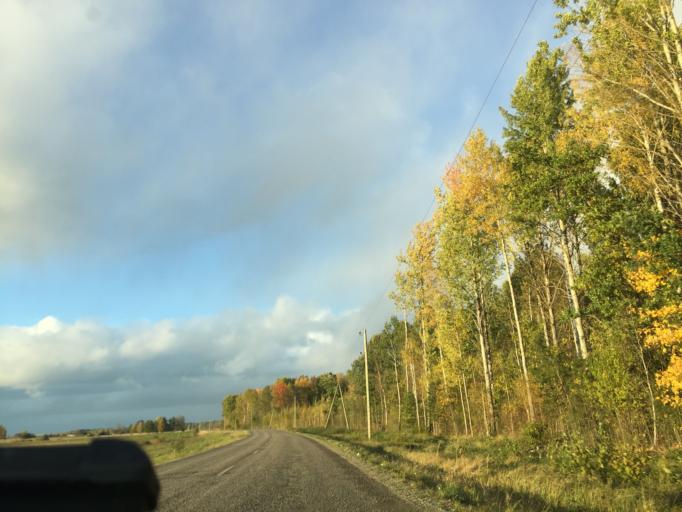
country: LV
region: Broceni
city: Broceni
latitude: 56.8680
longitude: 22.3823
